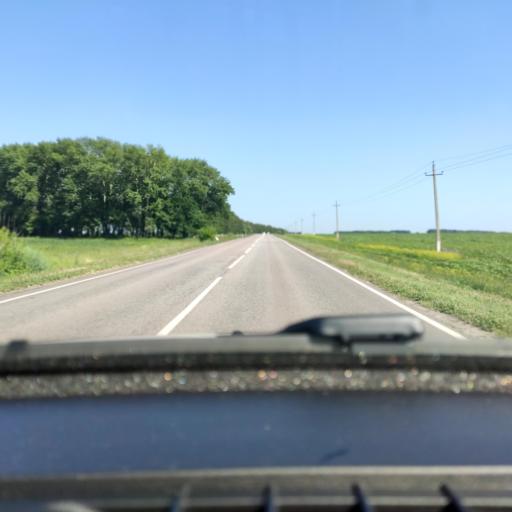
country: RU
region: Voronezj
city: Panino
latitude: 51.6570
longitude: 39.9978
